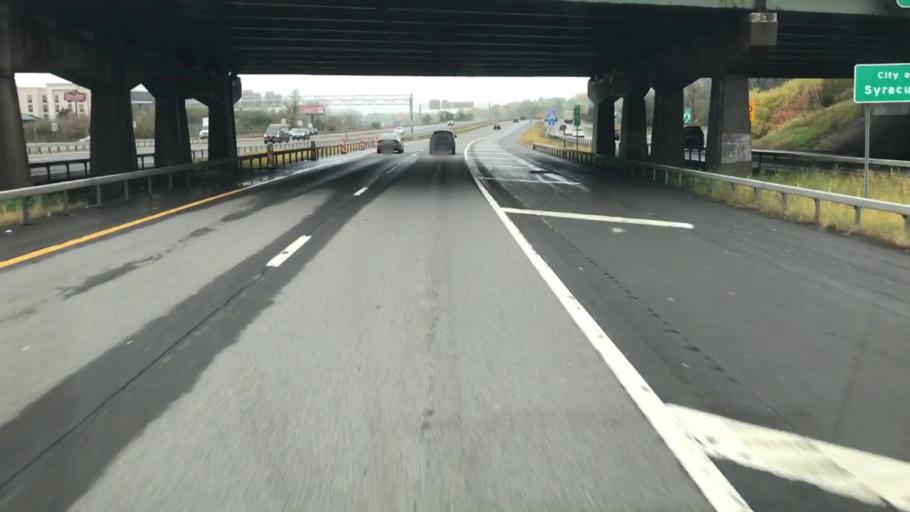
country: US
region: New York
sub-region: Onondaga County
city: East Syracuse
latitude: 43.0584
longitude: -76.0834
